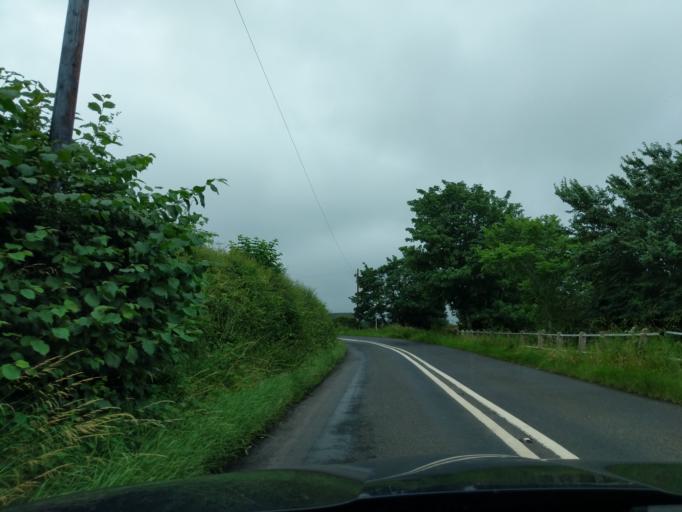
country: GB
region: England
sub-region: Northumberland
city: Ford
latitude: 55.6629
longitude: -2.1027
